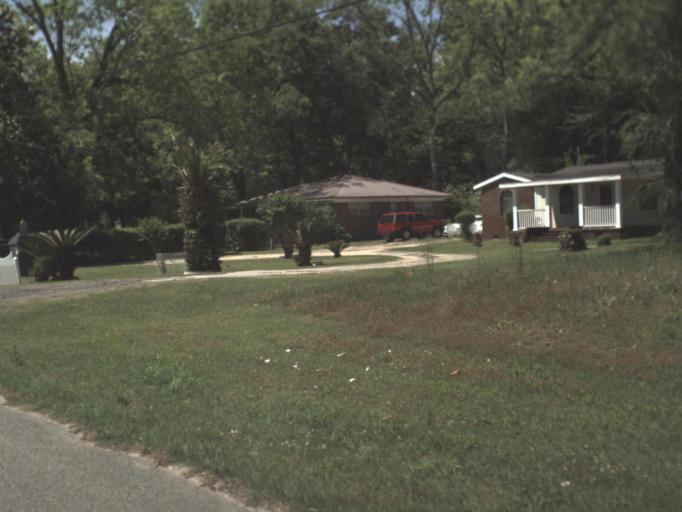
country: US
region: Florida
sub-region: Jackson County
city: Marianna
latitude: 30.7585
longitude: -85.2296
